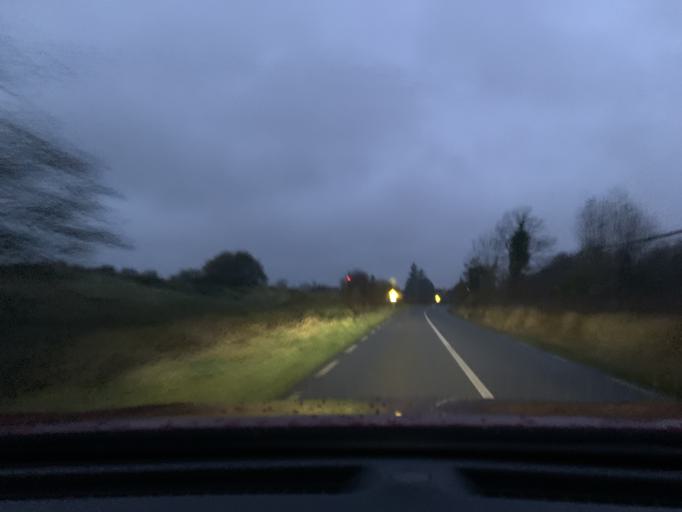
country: IE
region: Connaught
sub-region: Sligo
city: Ballymote
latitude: 54.0797
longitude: -8.5173
